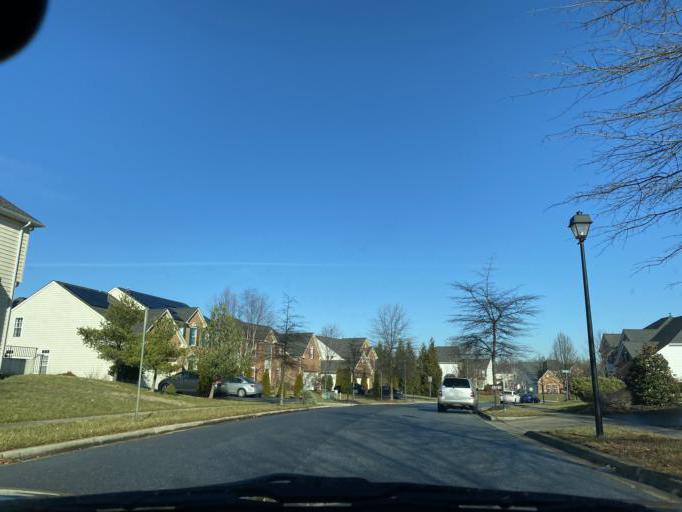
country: US
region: Maryland
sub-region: Prince George's County
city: Laurel
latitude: 39.0874
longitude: -76.8728
